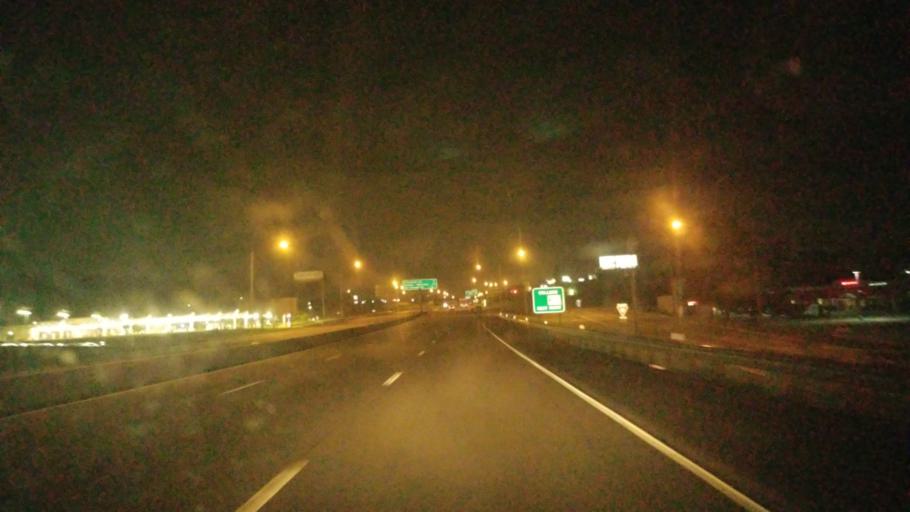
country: US
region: Missouri
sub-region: Saint Louis County
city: Black Jack
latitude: 38.7712
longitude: -90.2712
